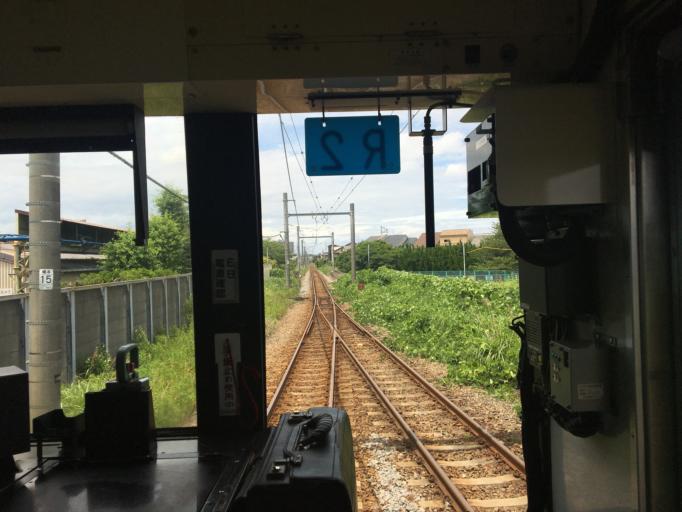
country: JP
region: Kanagawa
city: Chigasaki
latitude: 35.3410
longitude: 139.4066
